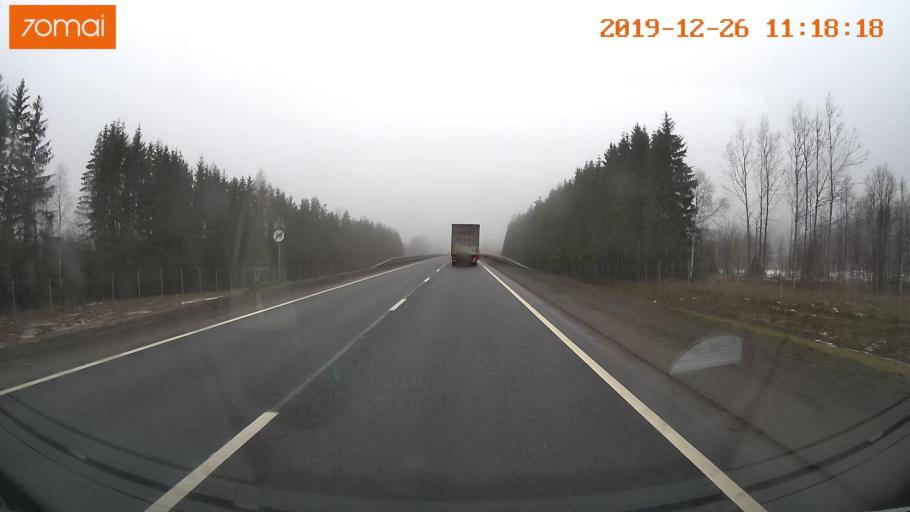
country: RU
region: Vologda
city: Chebsara
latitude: 59.1193
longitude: 39.0373
